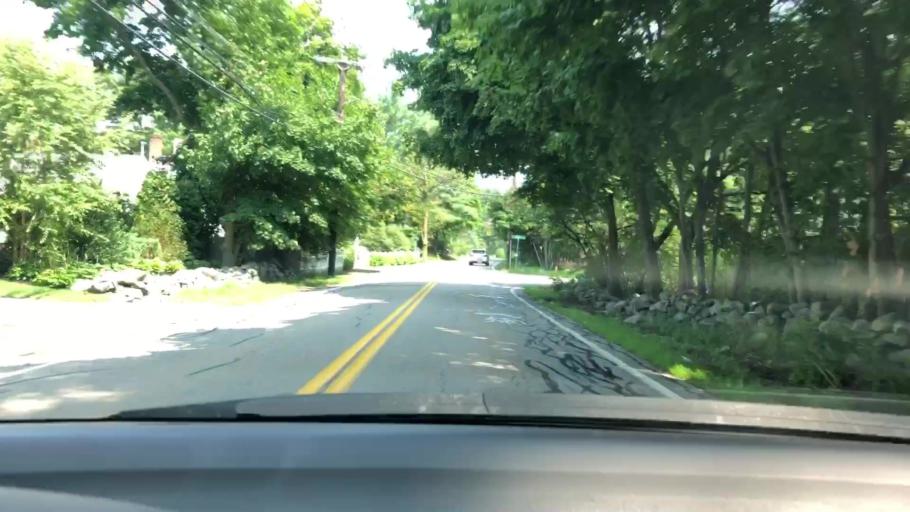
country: US
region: Massachusetts
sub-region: Norfolk County
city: Dedham
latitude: 42.2167
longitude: -71.1671
